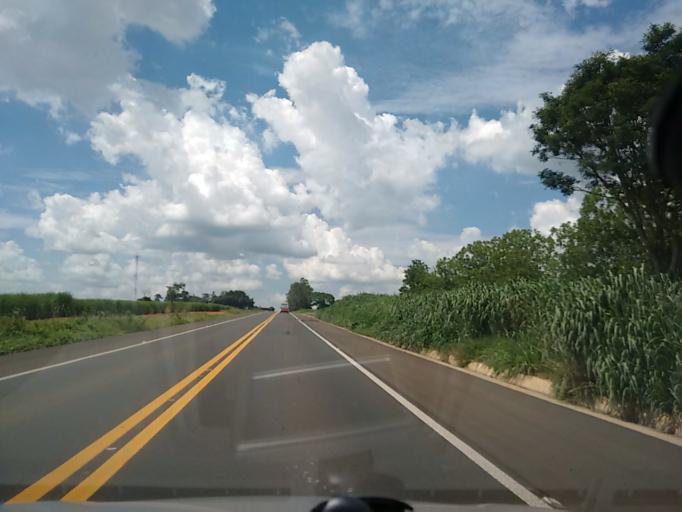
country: BR
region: Sao Paulo
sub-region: Osvaldo Cruz
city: Osvaldo Cruz
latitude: -21.9218
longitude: -50.9013
